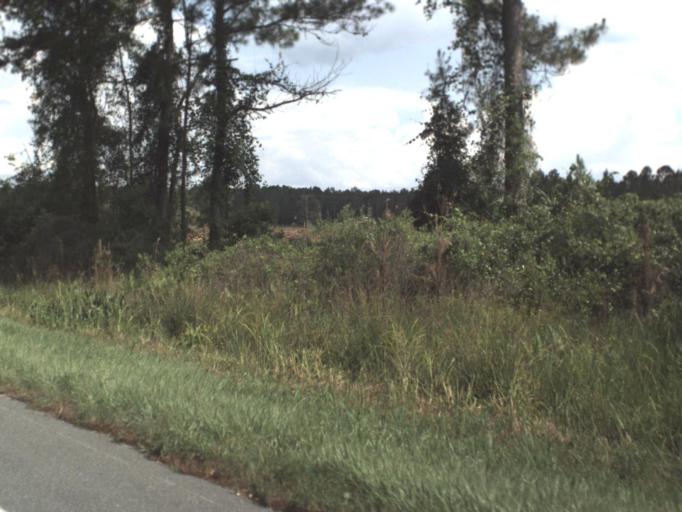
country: US
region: Florida
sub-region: Putnam County
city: Palatka
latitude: 29.6910
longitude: -81.7482
